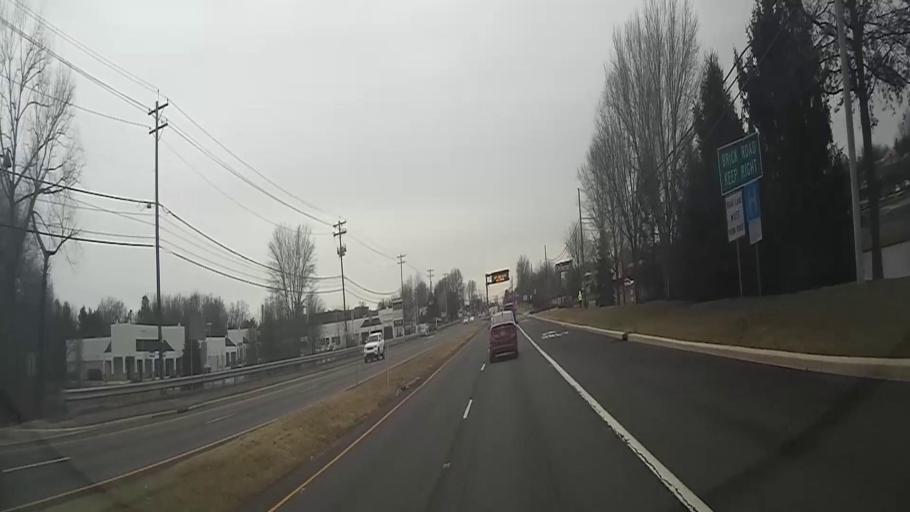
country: US
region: New Jersey
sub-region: Burlington County
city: Marlton
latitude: 39.8767
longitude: -74.9218
